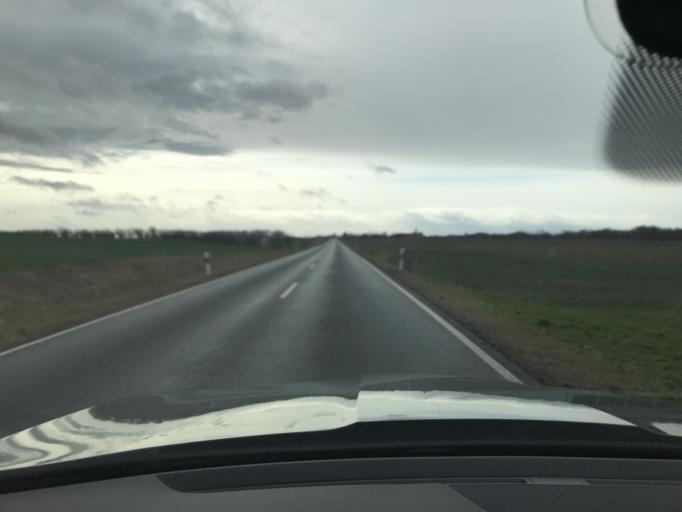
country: DE
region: Saxony-Anhalt
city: Groeningen
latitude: 51.9272
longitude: 11.2028
